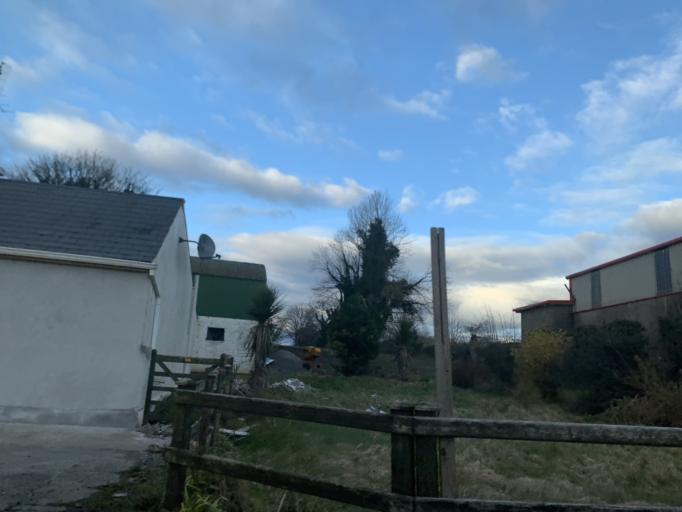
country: IE
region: Connaught
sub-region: Maigh Eo
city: Ballyhaunis
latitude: 53.8593
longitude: -8.7423
